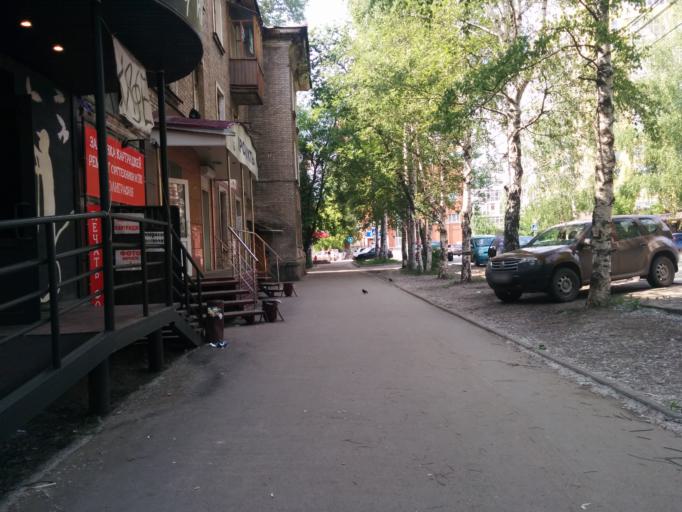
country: RU
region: Perm
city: Perm
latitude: 58.0207
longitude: 56.2897
